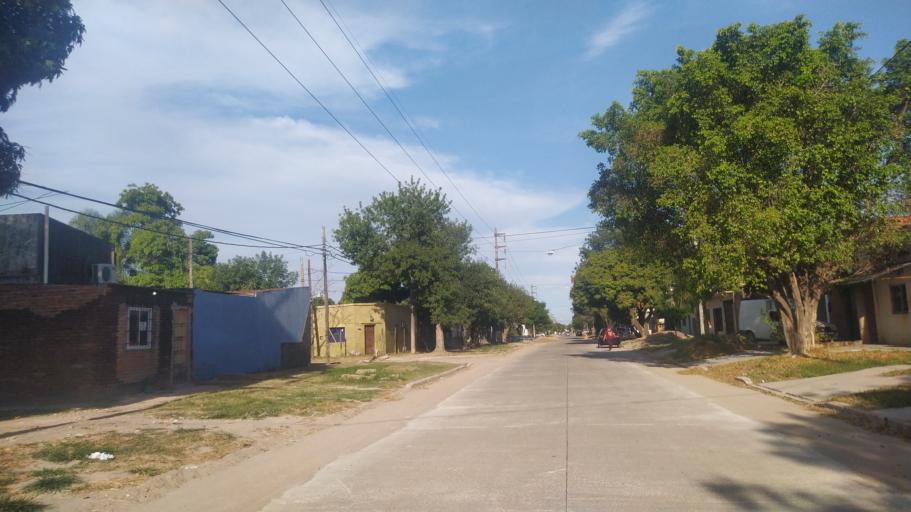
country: AR
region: Corrientes
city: Corrientes
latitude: -27.4817
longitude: -58.8051
